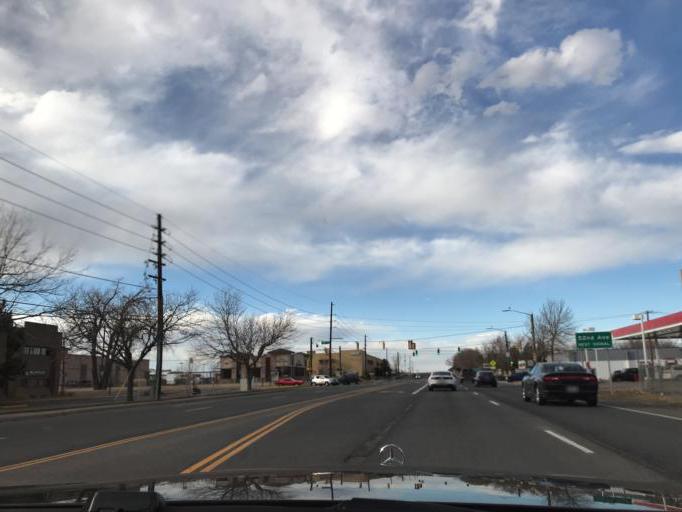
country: US
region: Colorado
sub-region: Jefferson County
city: Applewood
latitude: 39.7898
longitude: -105.1380
